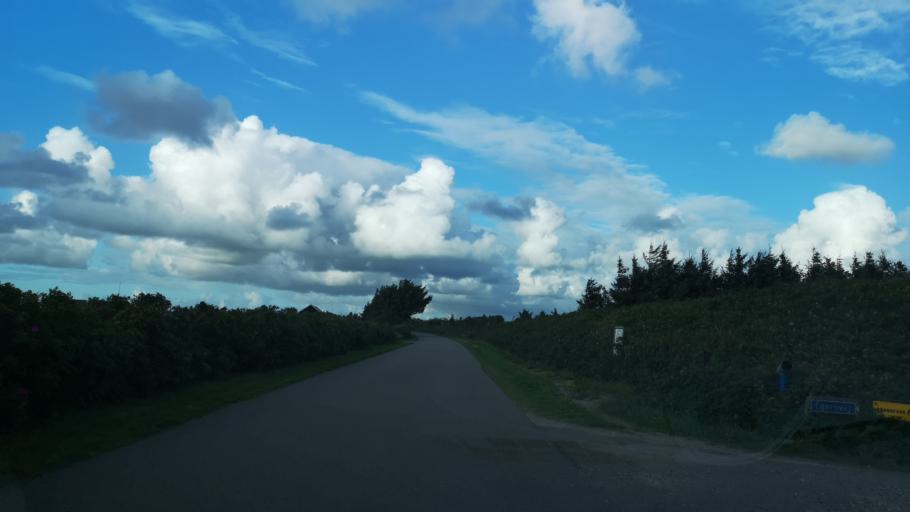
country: DK
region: Central Jutland
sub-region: Ringkobing-Skjern Kommune
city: Ringkobing
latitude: 56.1283
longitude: 8.1299
